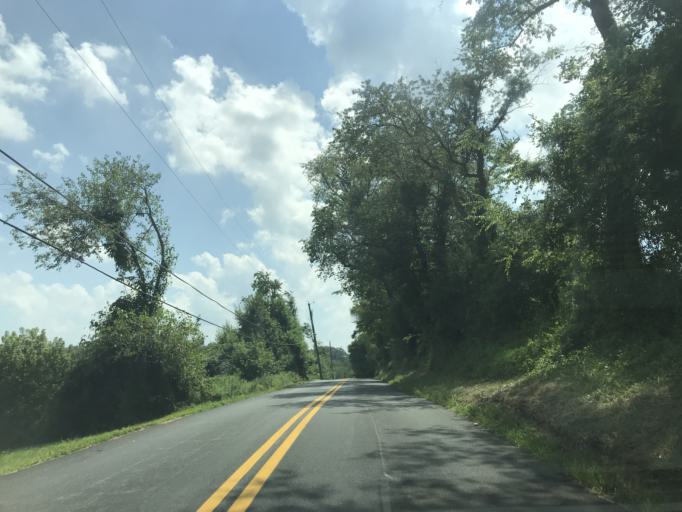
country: US
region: Maryland
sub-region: Carroll County
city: Hampstead
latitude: 39.6186
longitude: -76.7890
